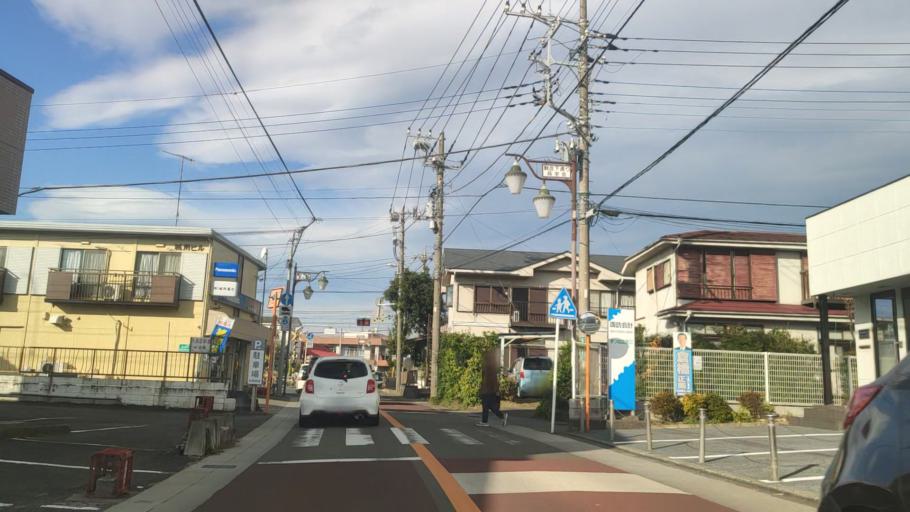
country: JP
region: Kanagawa
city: Zama
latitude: 35.4572
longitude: 139.3988
